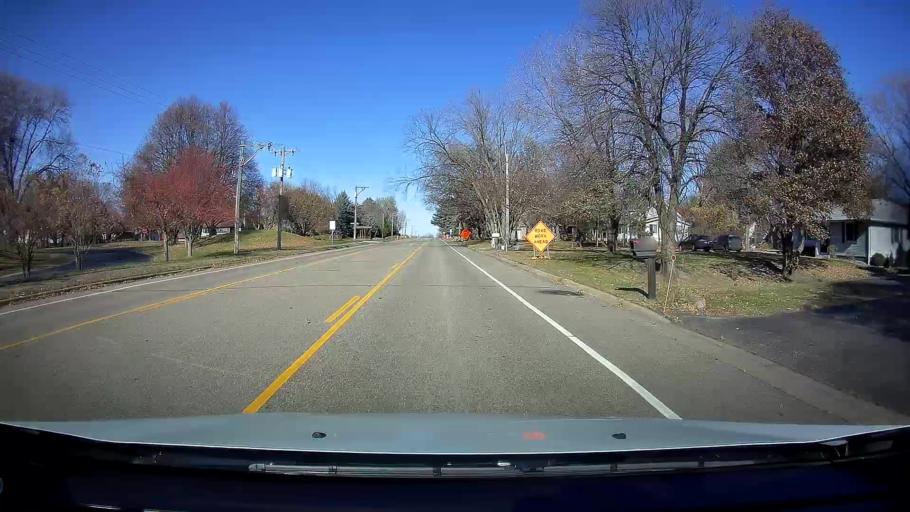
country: US
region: Minnesota
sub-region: Ramsey County
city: Shoreview
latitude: 45.0747
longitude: -93.1575
